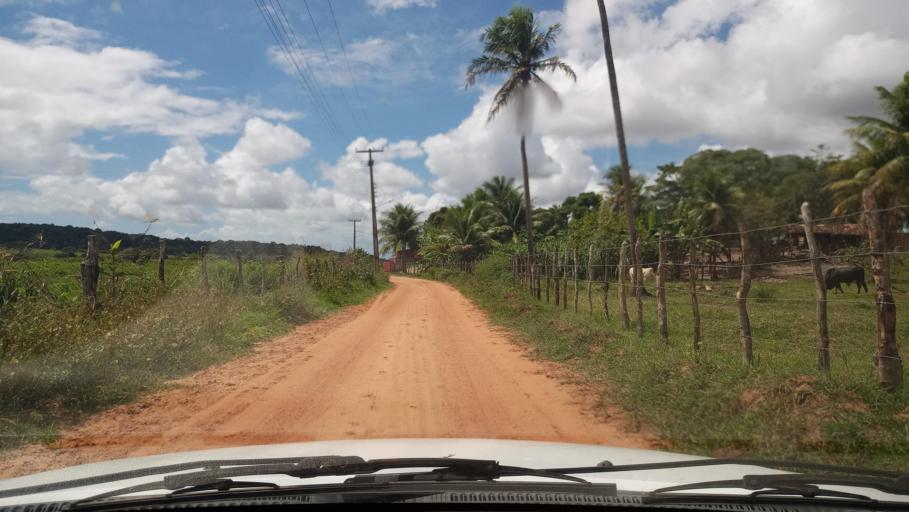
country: BR
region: Rio Grande do Norte
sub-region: Goianinha
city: Goianinha
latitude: -6.2613
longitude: -35.2556
